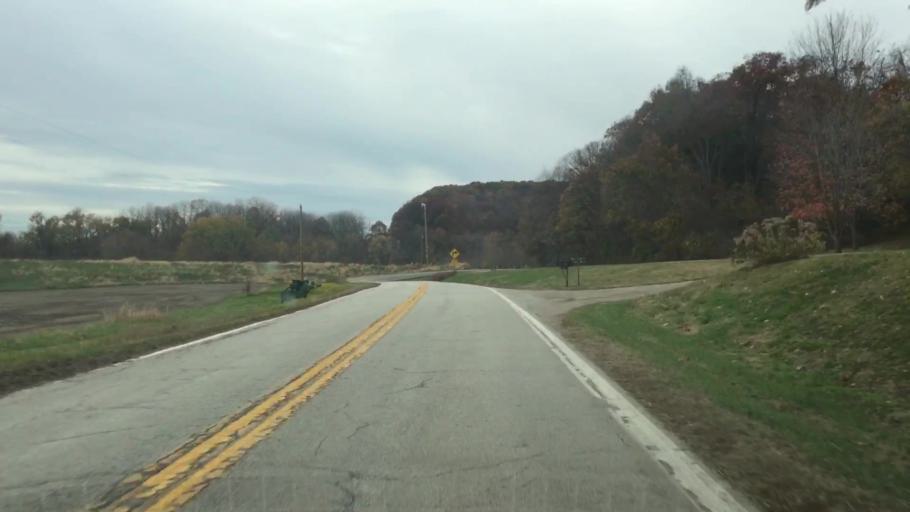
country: US
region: Missouri
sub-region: Gasconade County
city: Hermann
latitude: 38.7054
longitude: -91.6219
